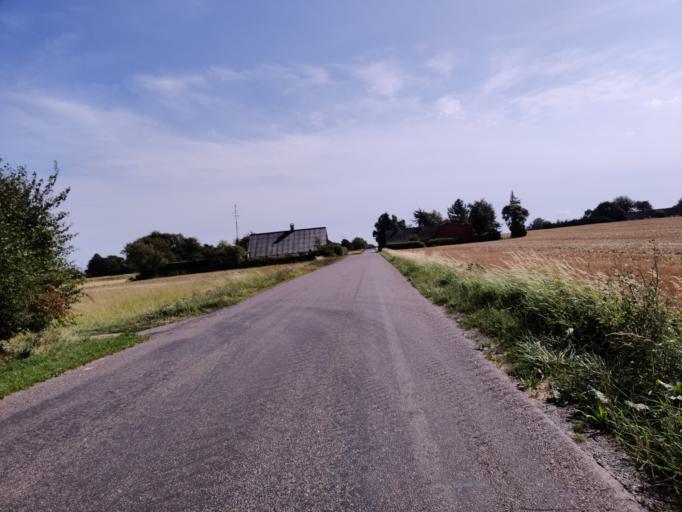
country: DK
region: Zealand
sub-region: Guldborgsund Kommune
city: Nykobing Falster
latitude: 54.6224
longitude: 11.9113
